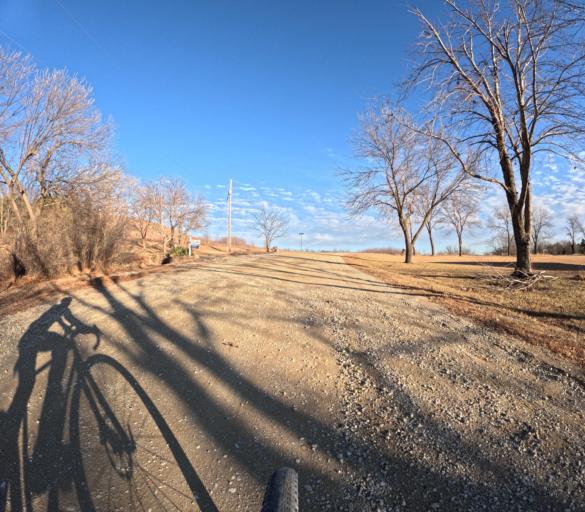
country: US
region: Kansas
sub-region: Riley County
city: Ogden
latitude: 39.2193
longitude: -96.6825
